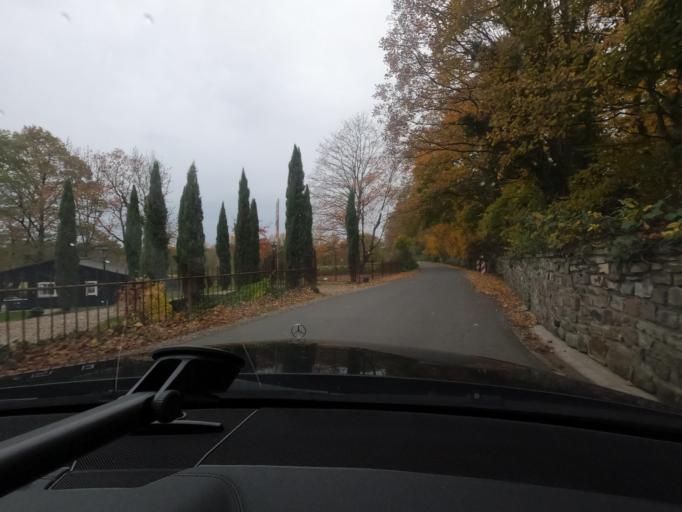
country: DE
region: North Rhine-Westphalia
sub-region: Regierungsbezirk Arnsberg
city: Mohnesee
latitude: 51.4833
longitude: 8.1976
